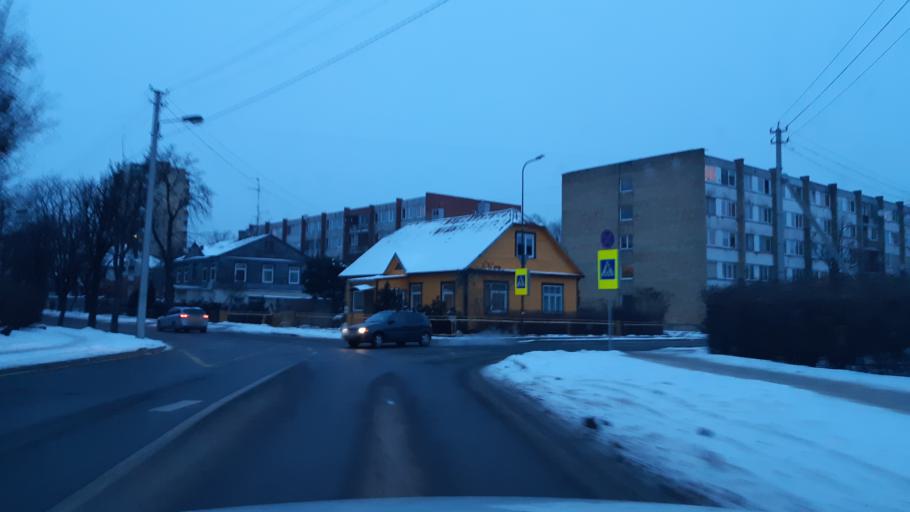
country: LT
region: Kauno apskritis
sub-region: Kaunas
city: Eiguliai
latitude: 54.9118
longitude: 23.9423
